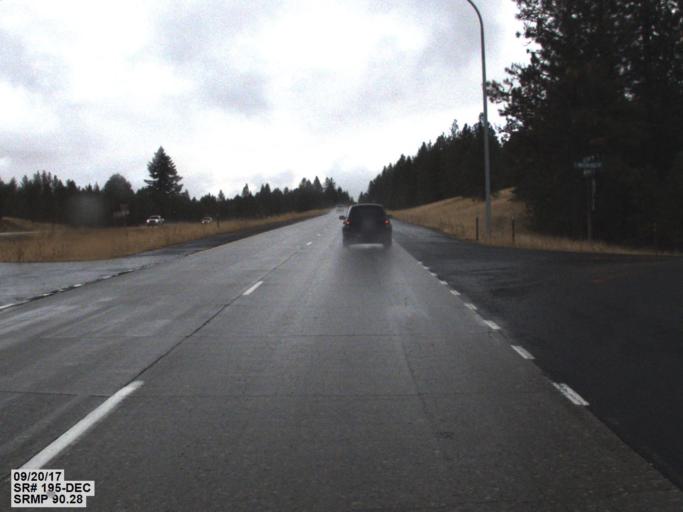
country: US
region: Washington
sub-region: Spokane County
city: Spokane
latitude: 47.5748
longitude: -117.4016
